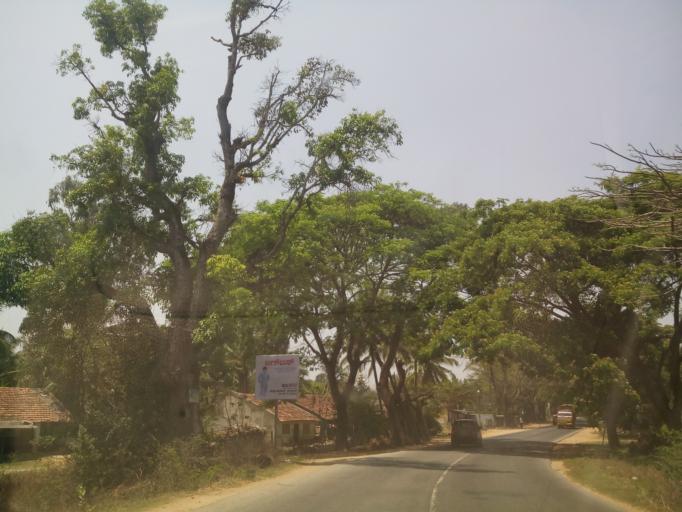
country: IN
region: Karnataka
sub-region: Hassan
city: Alur
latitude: 12.9767
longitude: 76.0168
